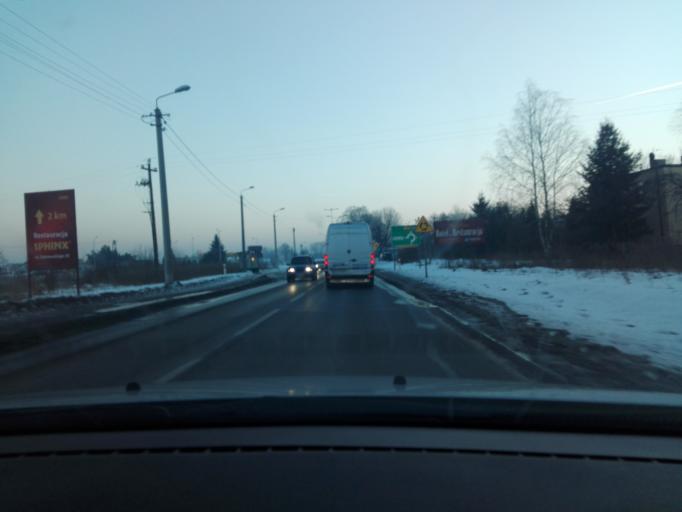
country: PL
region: Lodz Voivodeship
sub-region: Powiat zgierski
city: Zgierz
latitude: 51.8738
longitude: 19.4089
